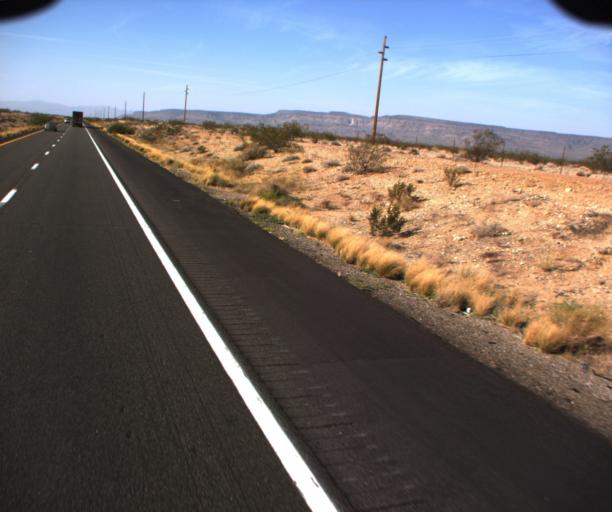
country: US
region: Arizona
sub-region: Mohave County
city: Kingman
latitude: 34.9803
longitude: -114.1408
